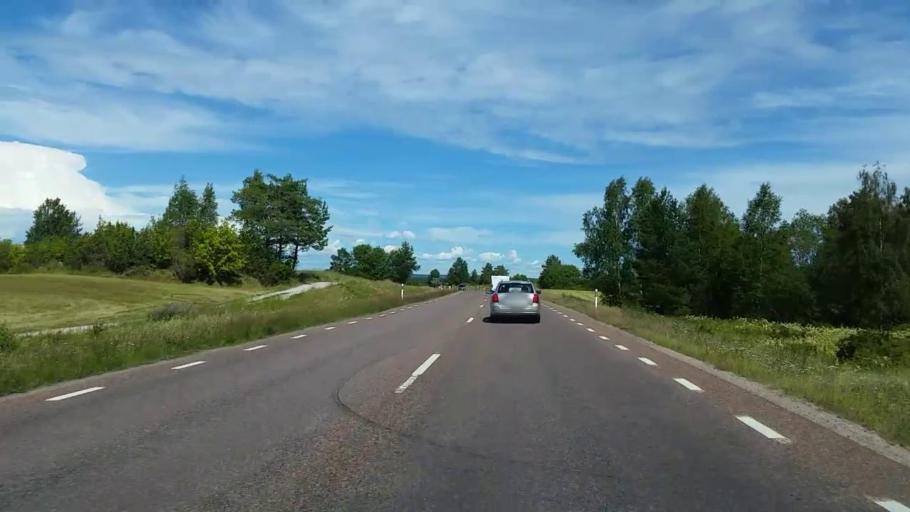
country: SE
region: Dalarna
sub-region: Rattviks Kommun
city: Raettvik
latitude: 60.9318
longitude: 15.2275
